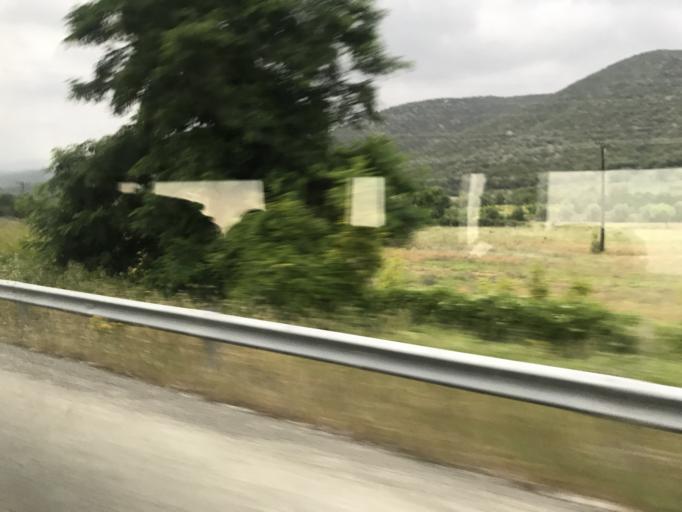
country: GR
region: East Macedonia and Thrace
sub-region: Nomos Rodopis
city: Iasmos
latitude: 41.1180
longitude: 25.1003
